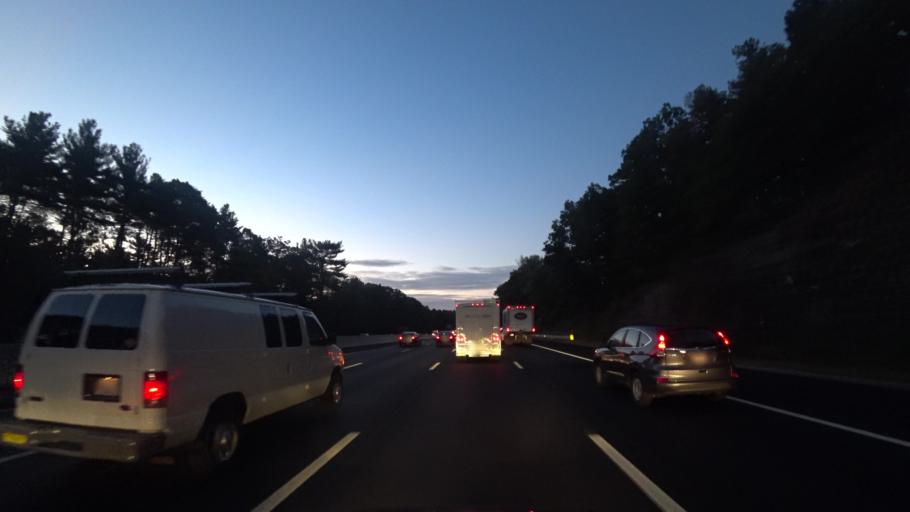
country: US
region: Massachusetts
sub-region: Middlesex County
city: Lexington
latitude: 42.4540
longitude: -71.2576
